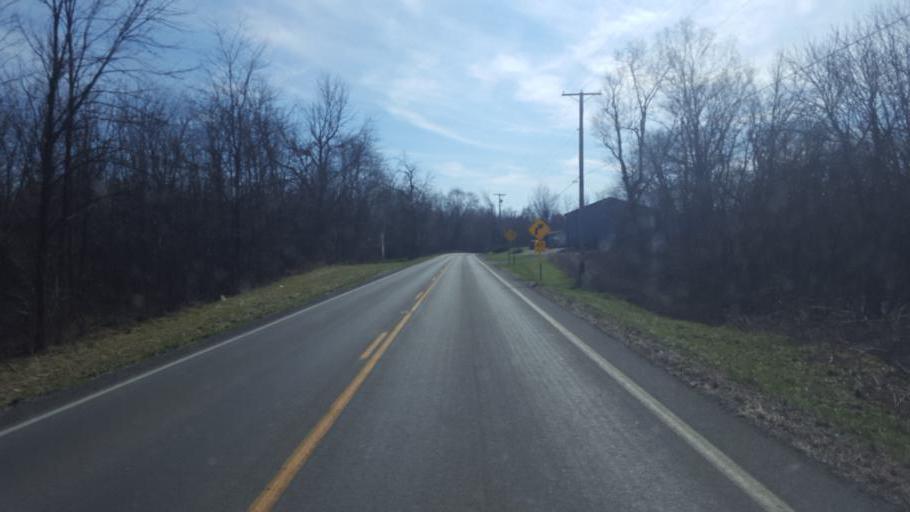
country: US
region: Ohio
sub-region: Hardin County
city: Forest
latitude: 40.7061
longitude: -83.3867
